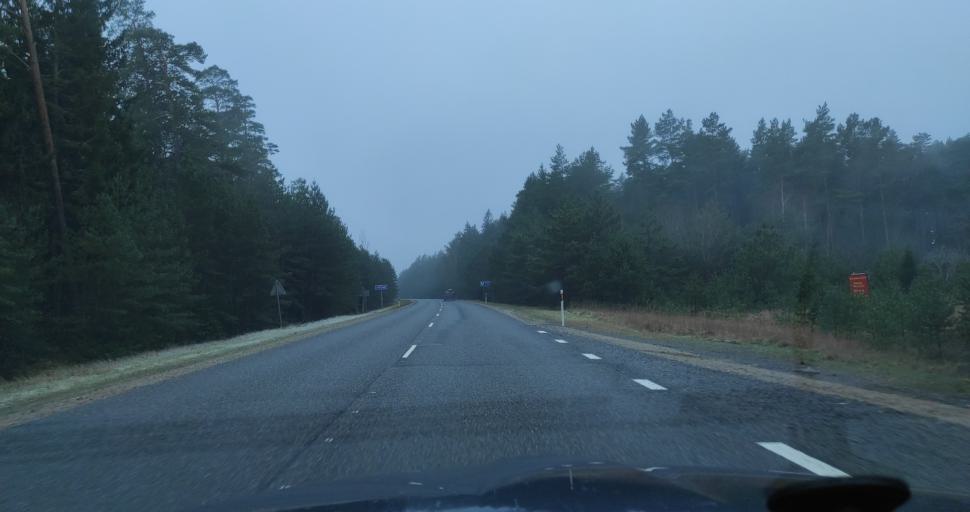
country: LV
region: Pavilostas
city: Pavilosta
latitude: 56.9703
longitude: 21.3444
